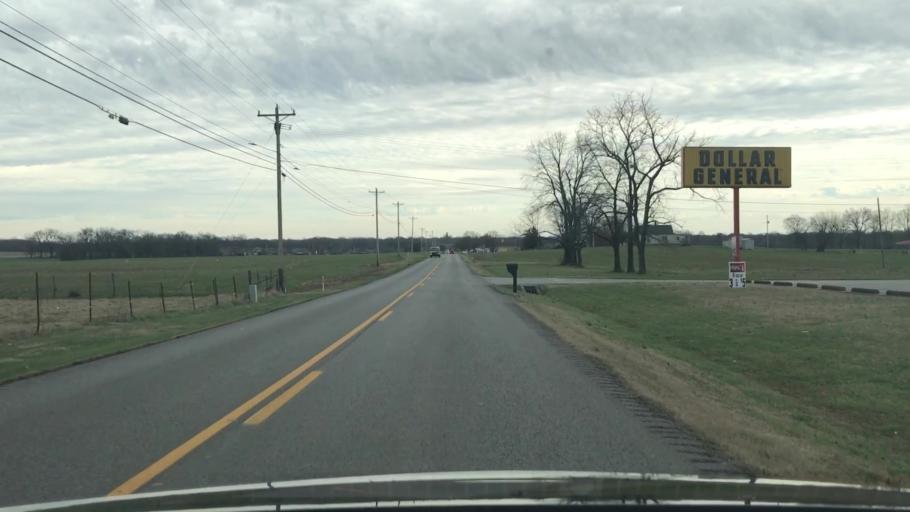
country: US
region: Kentucky
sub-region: Christian County
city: Hopkinsville
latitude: 36.8622
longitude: -87.5353
